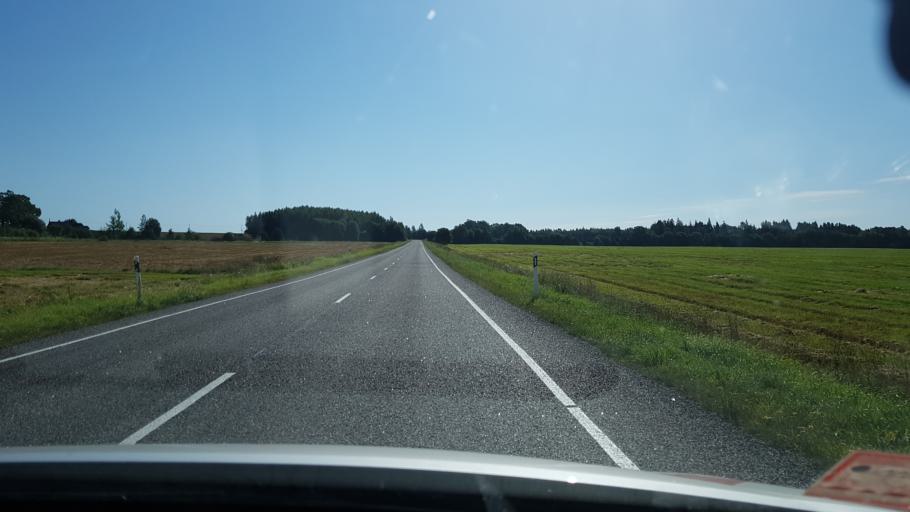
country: EE
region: Tartu
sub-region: Tartu linn
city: Tartu
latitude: 58.4669
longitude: 26.7377
